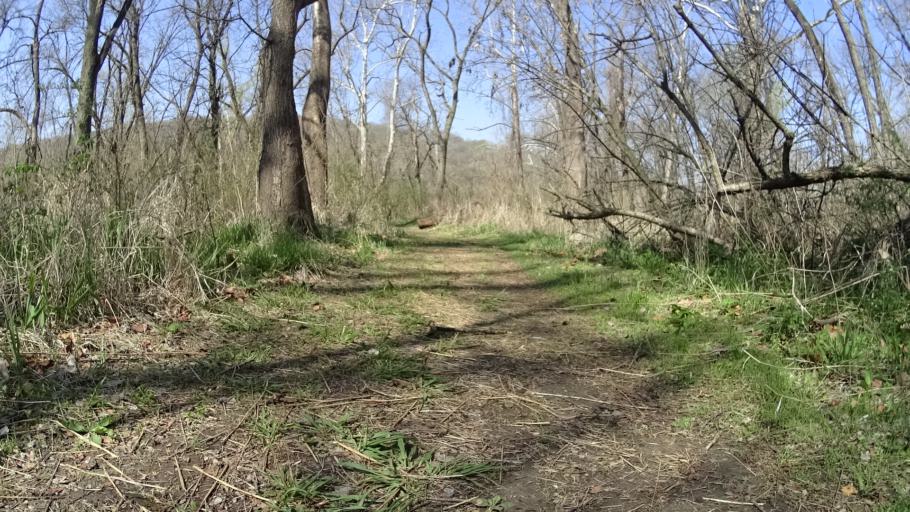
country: US
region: Nebraska
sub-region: Sarpy County
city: Bellevue
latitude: 41.1774
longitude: -95.8931
